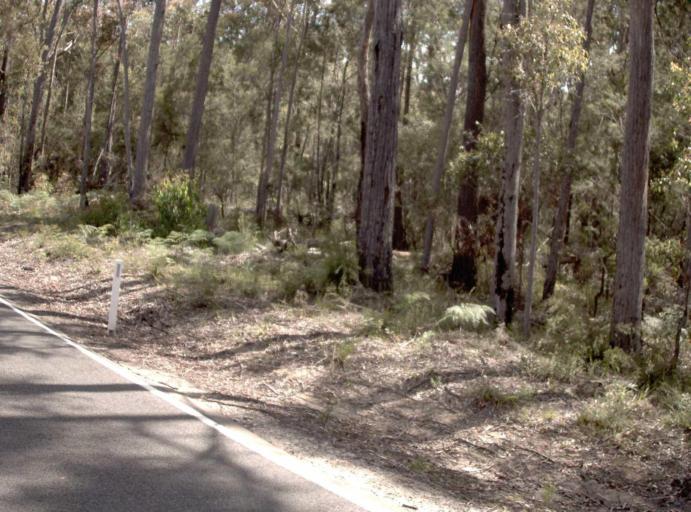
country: AU
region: New South Wales
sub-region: Bega Valley
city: Eden
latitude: -37.5355
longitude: 149.6971
